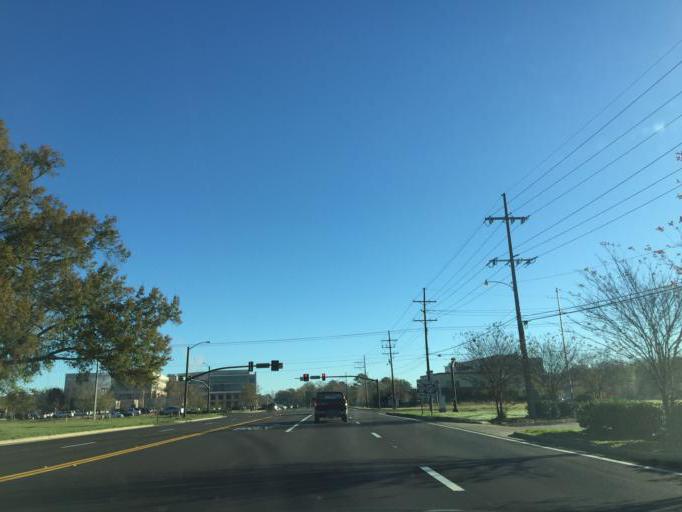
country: US
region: Mississippi
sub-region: Rankin County
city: Flowood
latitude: 32.3235
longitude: -90.1086
